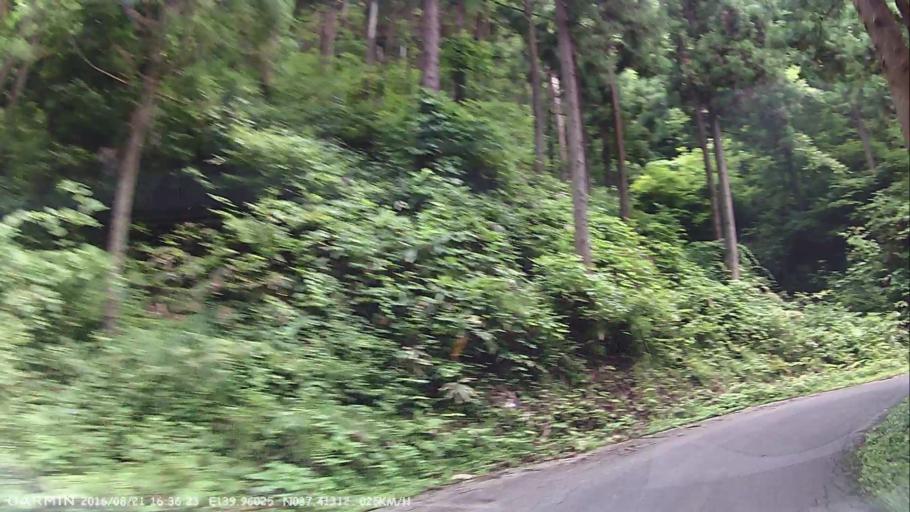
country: JP
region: Fukushima
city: Inawashiro
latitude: 37.4131
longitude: 139.9602
